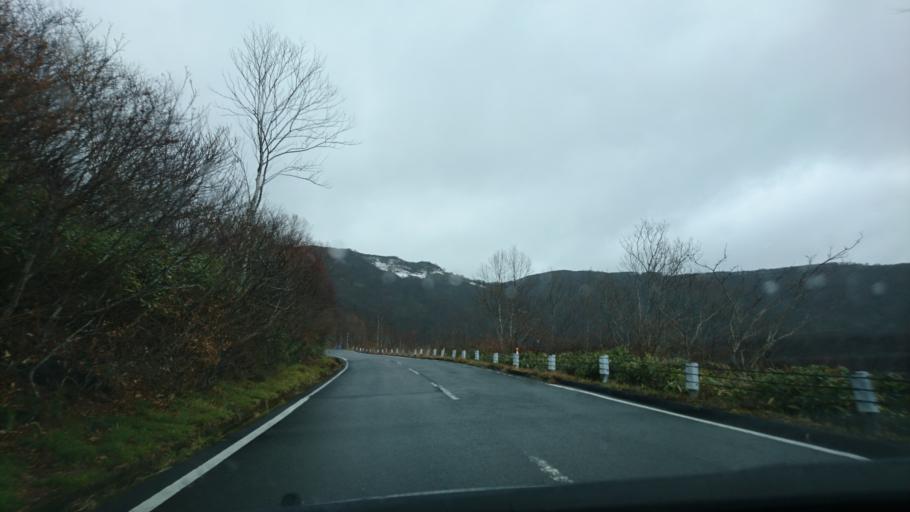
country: JP
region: Iwate
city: Ichinoseki
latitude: 38.9443
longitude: 140.8137
